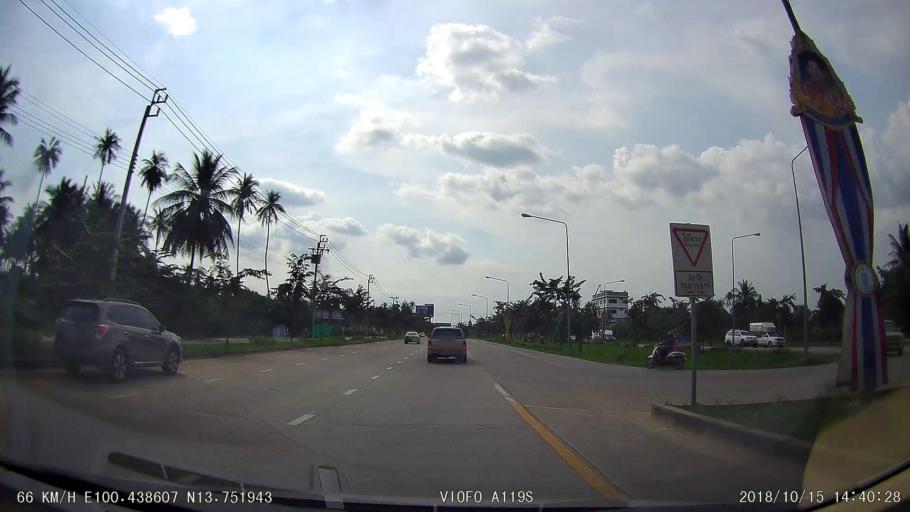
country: TH
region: Bangkok
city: Taling Chan
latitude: 13.7520
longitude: 100.4384
